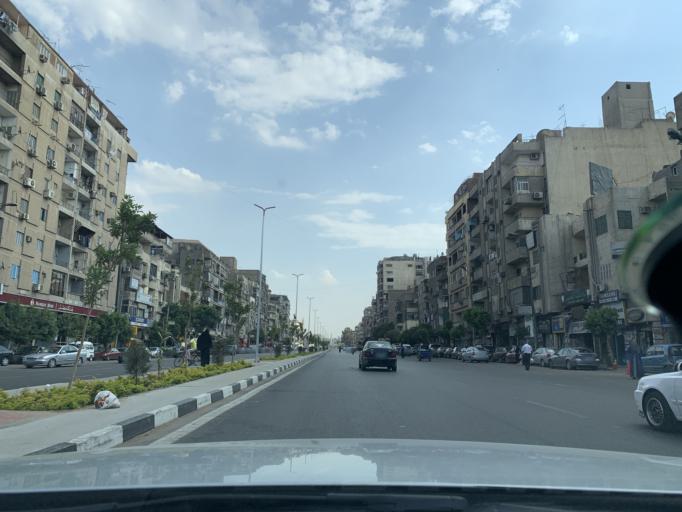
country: EG
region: Muhafazat al Qahirah
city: Cairo
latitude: 30.1043
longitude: 31.3436
